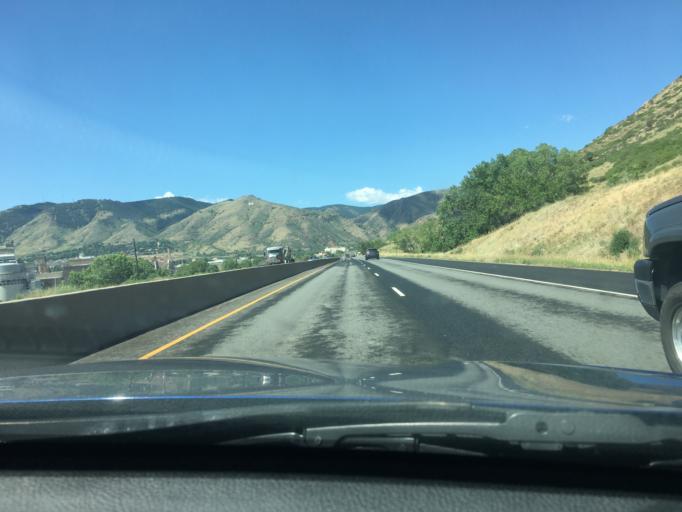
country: US
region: Colorado
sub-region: Jefferson County
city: Golden
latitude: 39.7676
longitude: -105.2079
